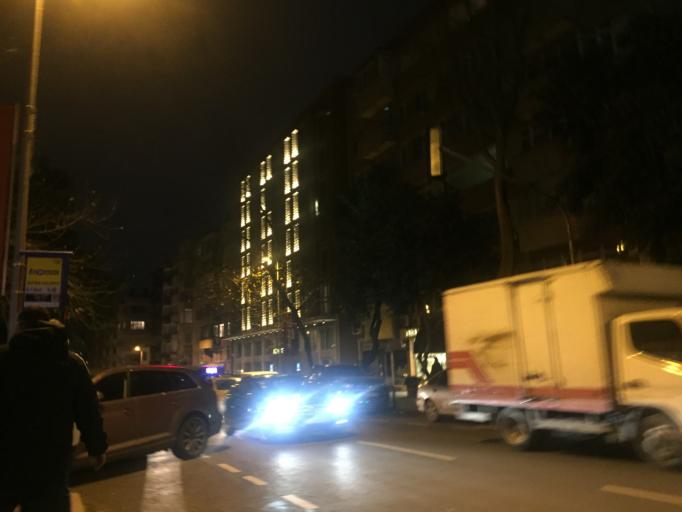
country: TR
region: Istanbul
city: Sisli
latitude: 41.0431
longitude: 28.9983
